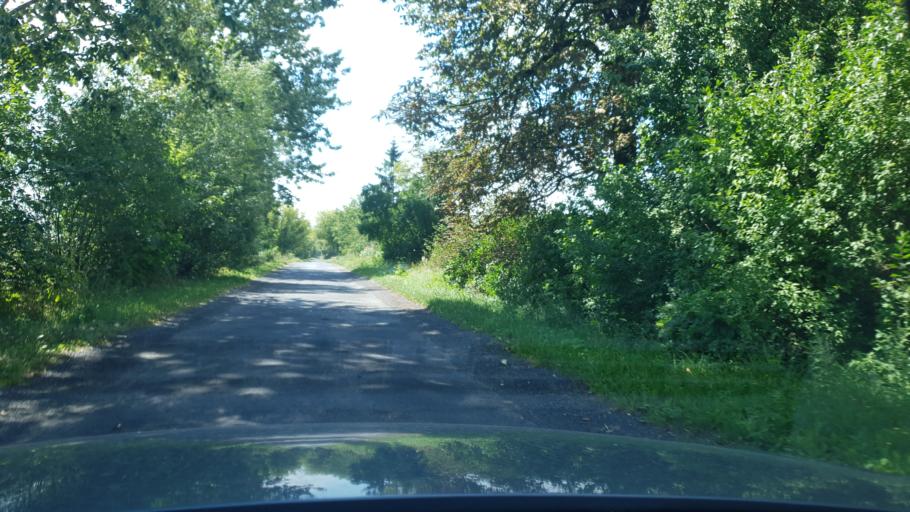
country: PL
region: Kujawsko-Pomorskie
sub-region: Powiat wabrzeski
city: Pluznica
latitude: 53.3102
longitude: 18.8194
